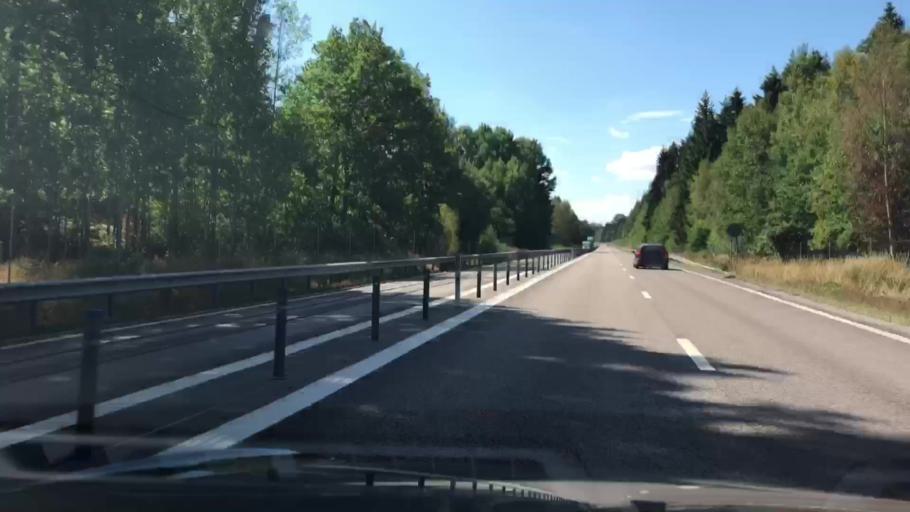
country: SE
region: Kalmar
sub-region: Monsteras Kommun
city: Timmernabben
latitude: 56.9413
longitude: 16.3889
